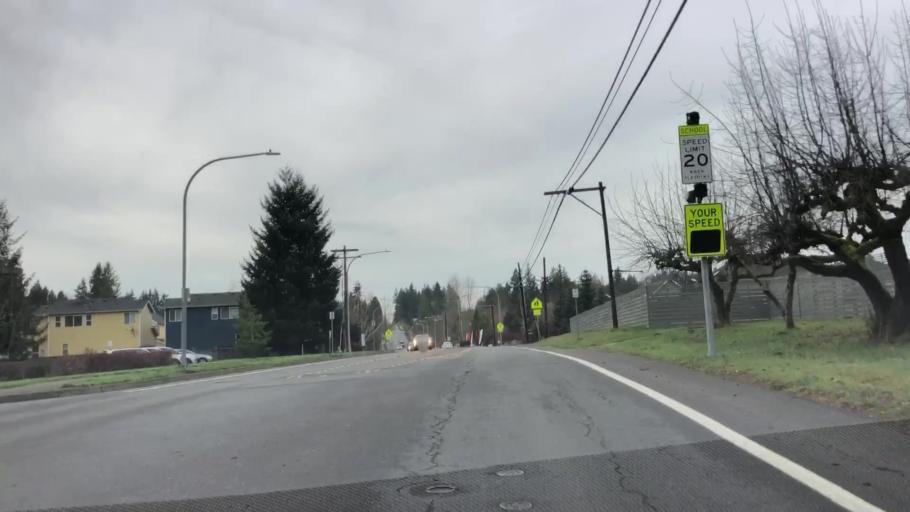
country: US
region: Washington
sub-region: King County
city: Redmond
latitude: 47.7036
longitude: -122.0988
